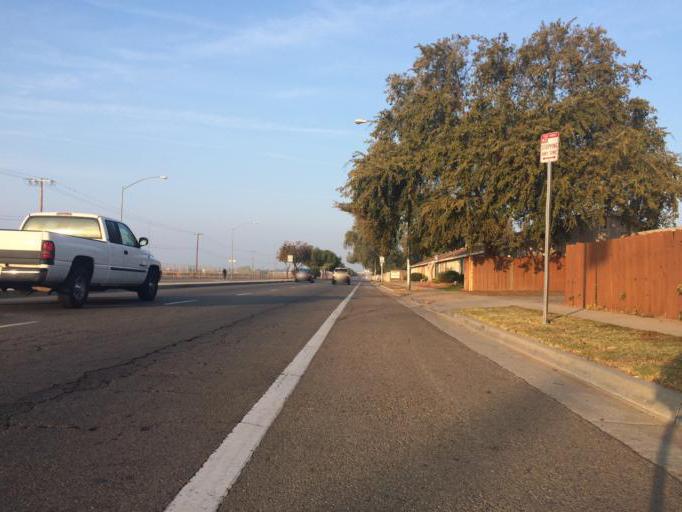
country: US
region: California
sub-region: Fresno County
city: Tarpey Village
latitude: 36.7943
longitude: -119.7366
